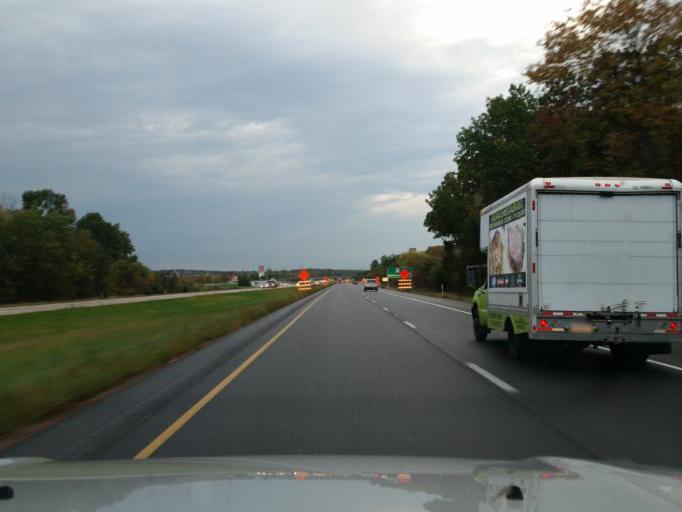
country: US
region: Pennsylvania
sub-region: Adams County
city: Lake Heritage
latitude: 39.8051
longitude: -77.1968
